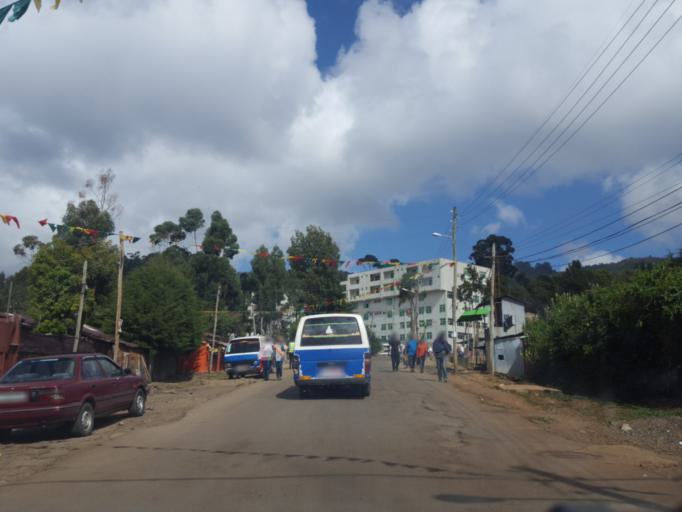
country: ET
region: Adis Abeba
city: Addis Ababa
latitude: 9.0726
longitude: 38.7593
